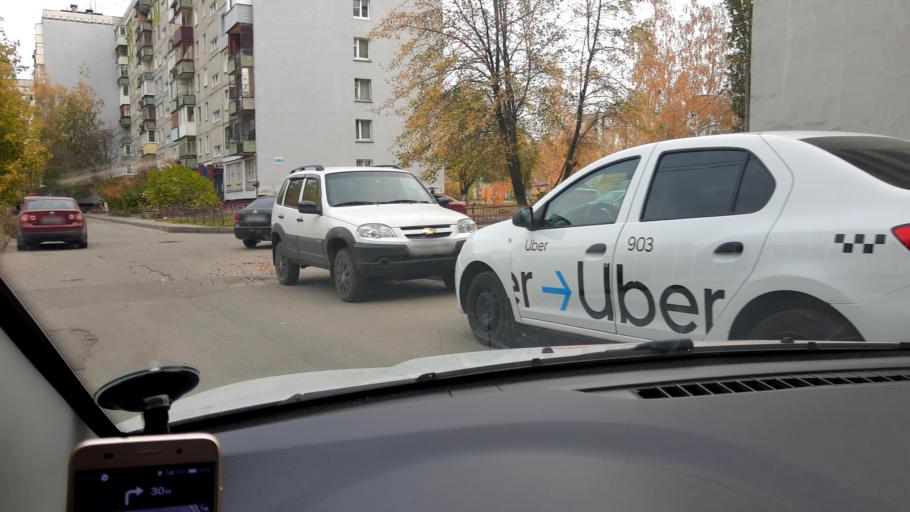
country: RU
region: Nizjnij Novgorod
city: Gorbatovka
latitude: 56.2709
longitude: 43.8768
